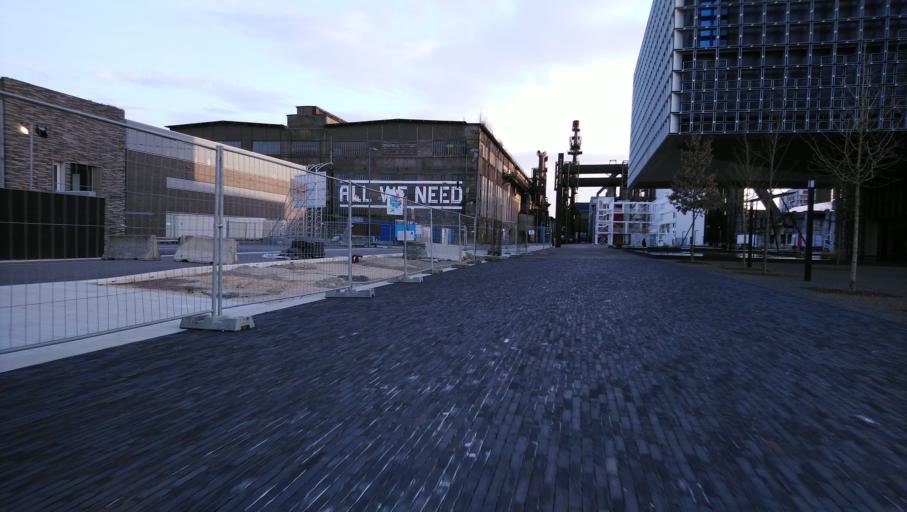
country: FR
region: Lorraine
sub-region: Departement de la Moselle
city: Russange
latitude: 49.5045
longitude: 5.9505
